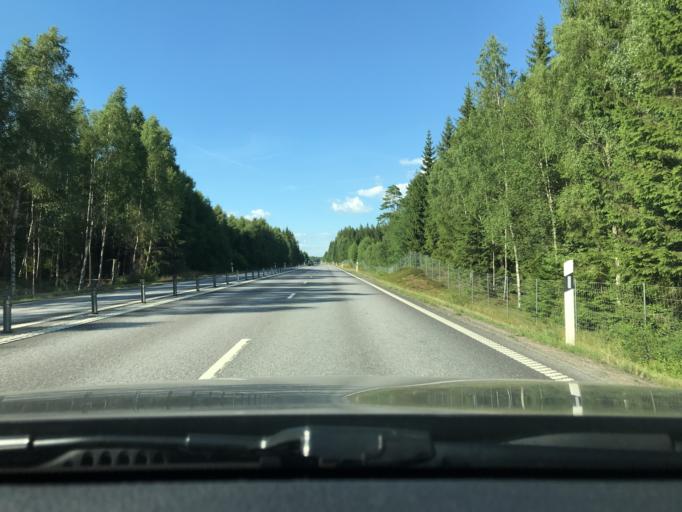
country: SE
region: Skane
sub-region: Osby Kommun
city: Osby
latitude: 56.4195
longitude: 14.0524
